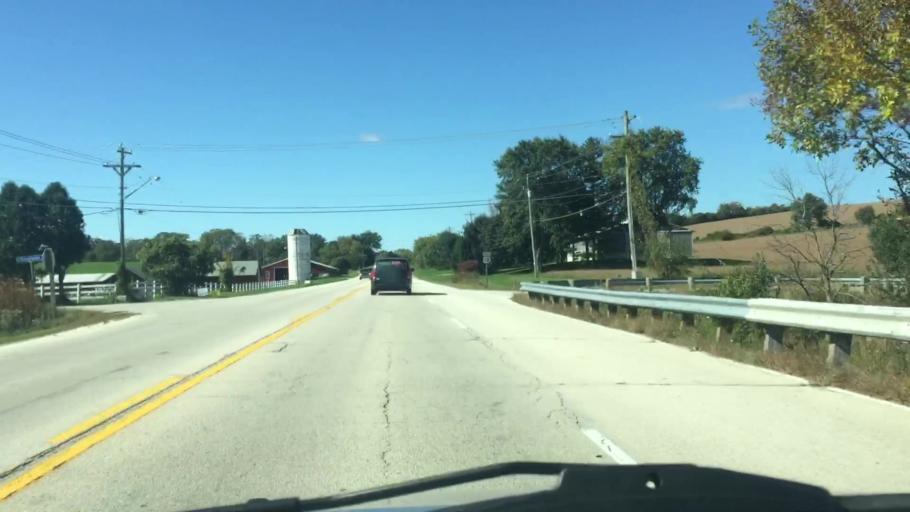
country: US
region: Wisconsin
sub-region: Waukesha County
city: Wales
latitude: 43.0205
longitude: -88.3440
